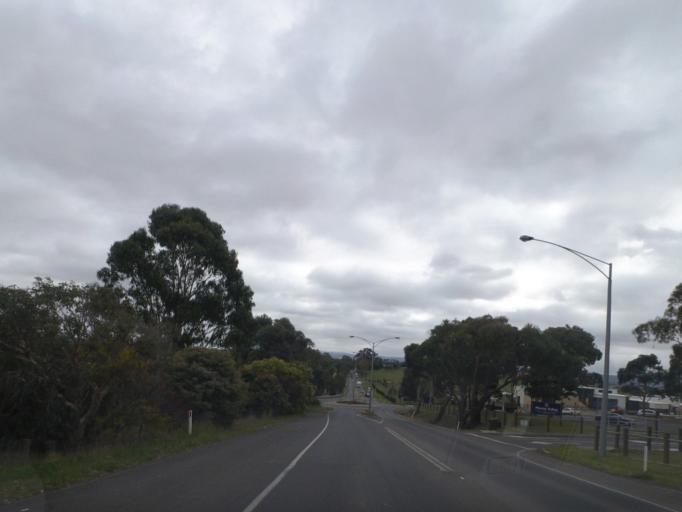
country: AU
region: Victoria
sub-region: Nillumbik
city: Doreen
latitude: -37.6138
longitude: 145.1368
